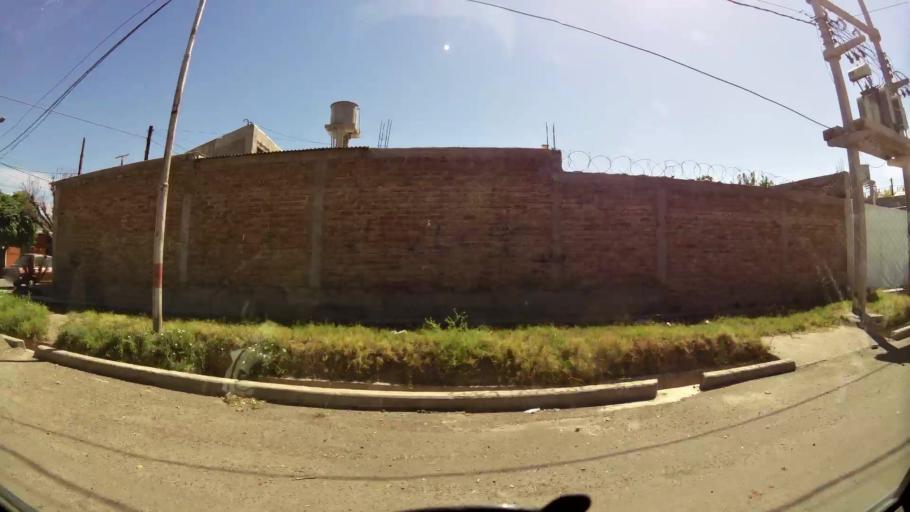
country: AR
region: Mendoza
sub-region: Departamento de Godoy Cruz
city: Godoy Cruz
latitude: -32.9669
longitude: -68.8367
